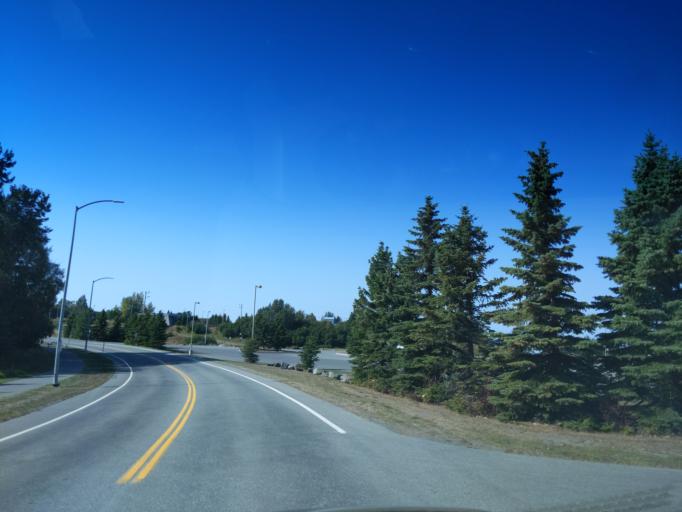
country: US
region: Alaska
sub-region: Anchorage Municipality
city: Anchorage
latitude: 61.1546
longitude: -150.0480
